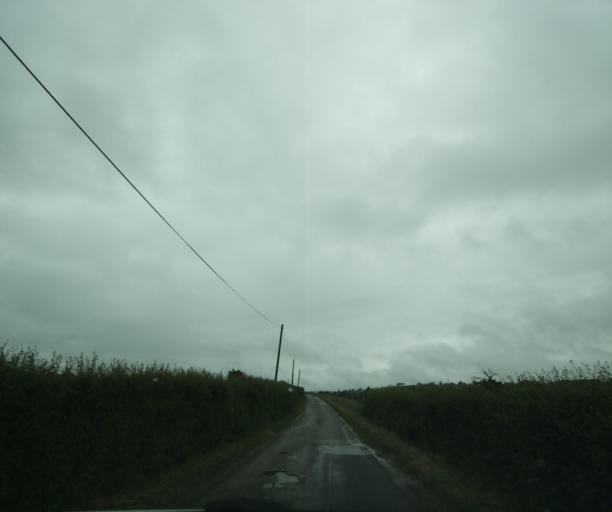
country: FR
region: Bourgogne
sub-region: Departement de Saone-et-Loire
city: Charolles
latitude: 46.3760
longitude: 4.2231
